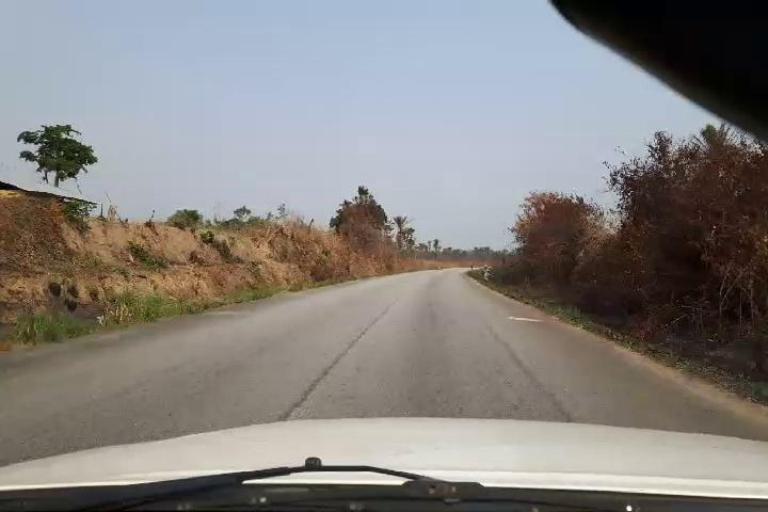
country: SL
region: Southern Province
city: Baiima
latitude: 8.1405
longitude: -11.8988
